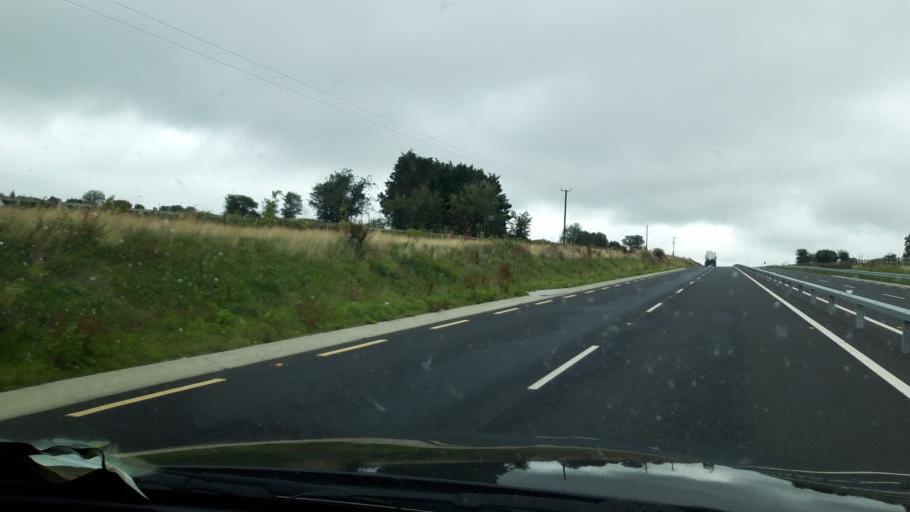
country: IE
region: Leinster
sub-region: Loch Garman
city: New Ross
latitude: 52.3901
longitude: -6.8846
